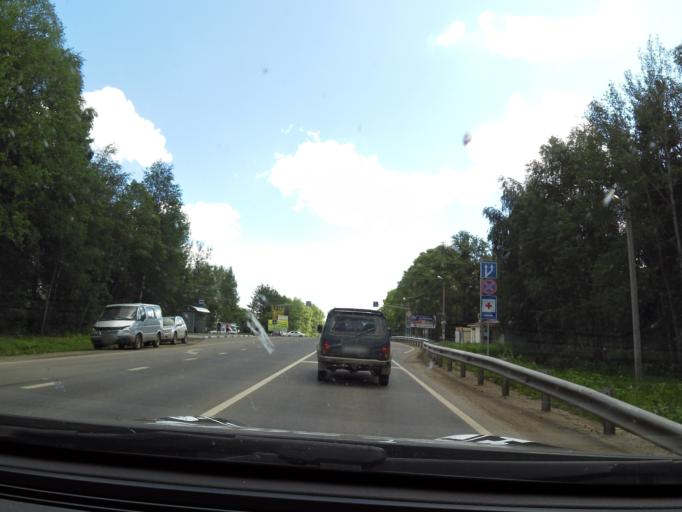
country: RU
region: Vologda
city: Molochnoye
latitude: 59.2608
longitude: 39.7480
